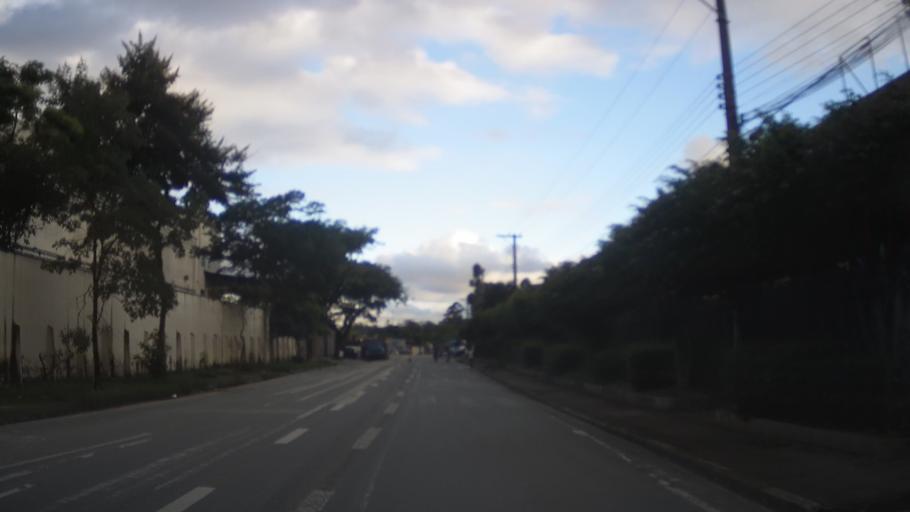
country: BR
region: Sao Paulo
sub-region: Guarulhos
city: Guarulhos
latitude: -23.4727
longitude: -46.4611
